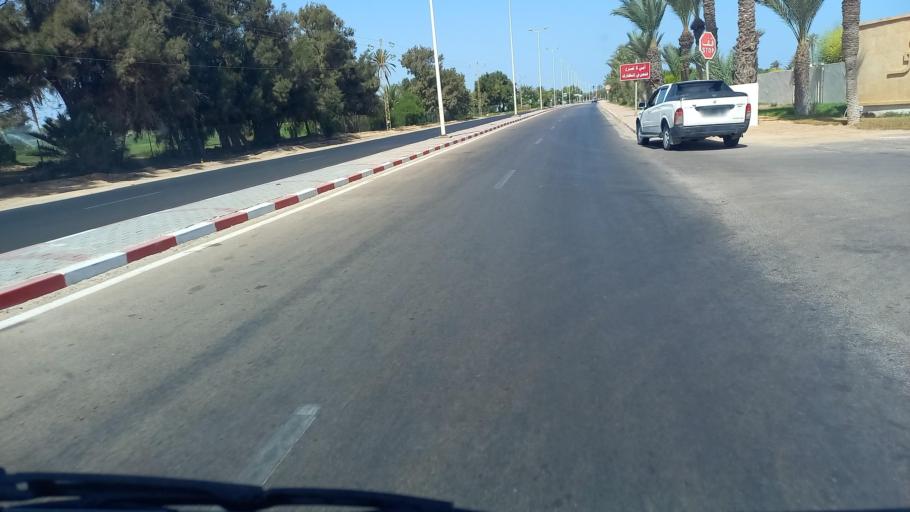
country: TN
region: Madanin
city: Midoun
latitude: 33.8267
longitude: 11.0149
